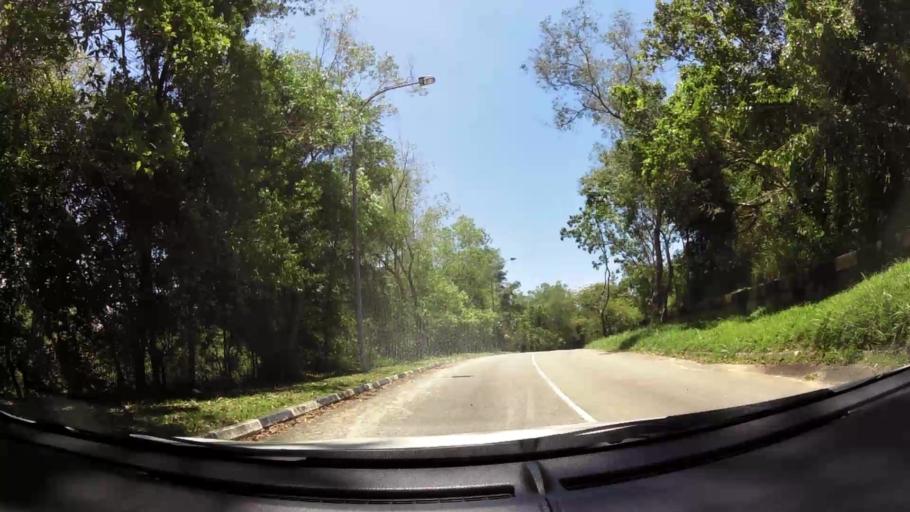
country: BN
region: Brunei and Muara
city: Bandar Seri Begawan
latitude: 4.9228
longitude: 114.9605
